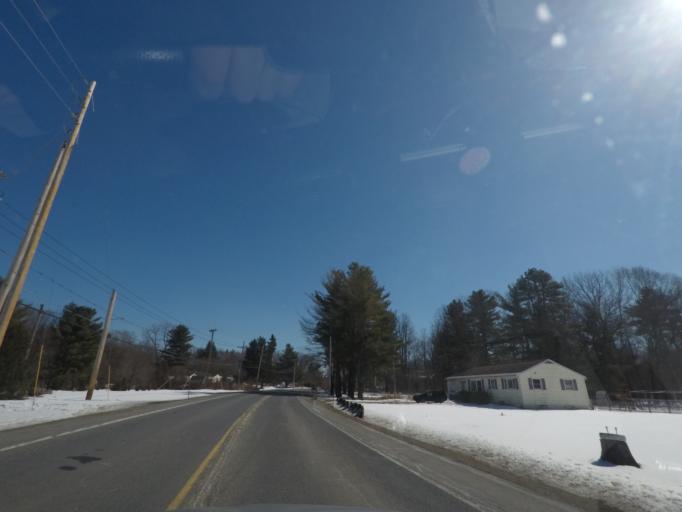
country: US
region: New York
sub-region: Saratoga County
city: Stillwater
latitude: 42.9073
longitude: -73.6054
